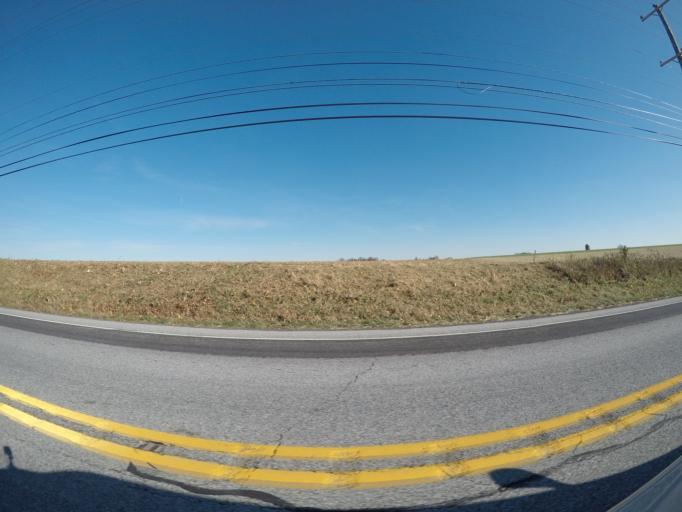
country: US
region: Pennsylvania
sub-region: Chester County
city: Oxford
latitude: 39.8547
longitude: -75.9330
